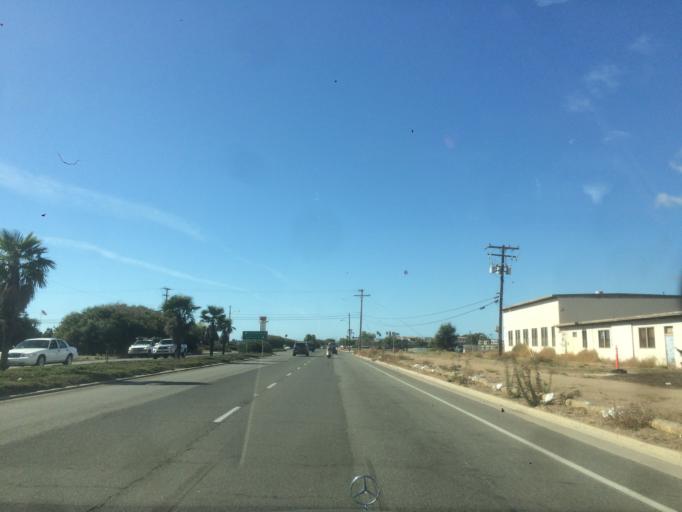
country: US
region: California
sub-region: Santa Barbara County
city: Goleta
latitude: 34.4340
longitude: -119.8369
